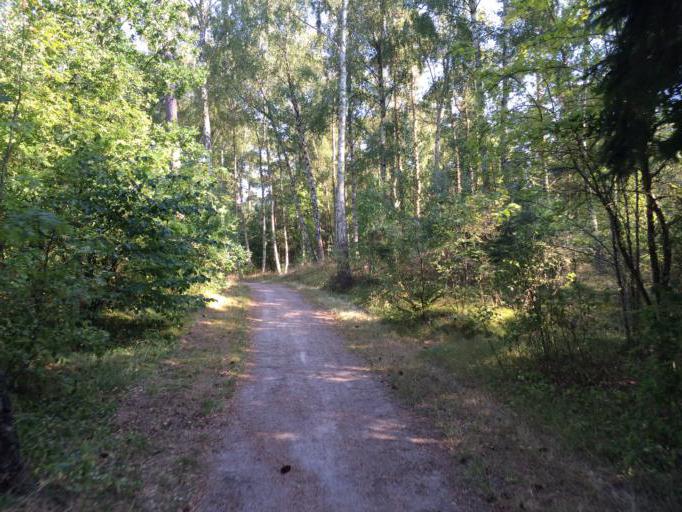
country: SE
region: Skane
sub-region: Vellinge Kommun
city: Skanor med Falsterbo
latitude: 55.4105
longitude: 12.8462
